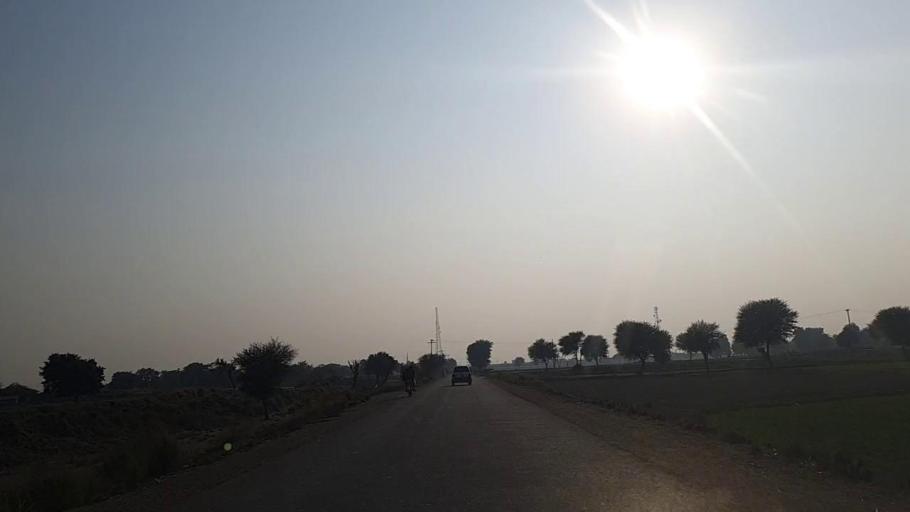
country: PK
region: Sindh
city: Shahpur Chakar
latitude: 26.2040
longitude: 68.5594
